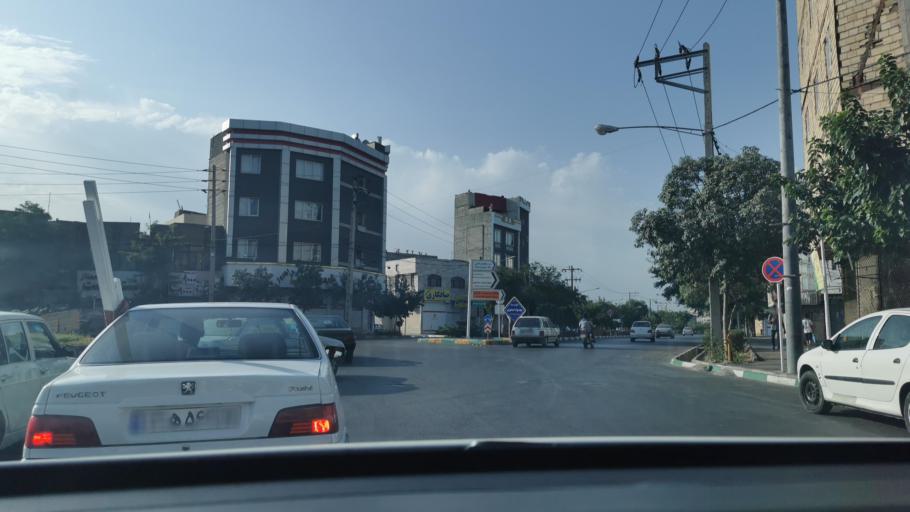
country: IR
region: Razavi Khorasan
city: Mashhad
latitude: 36.2900
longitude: 59.6500
